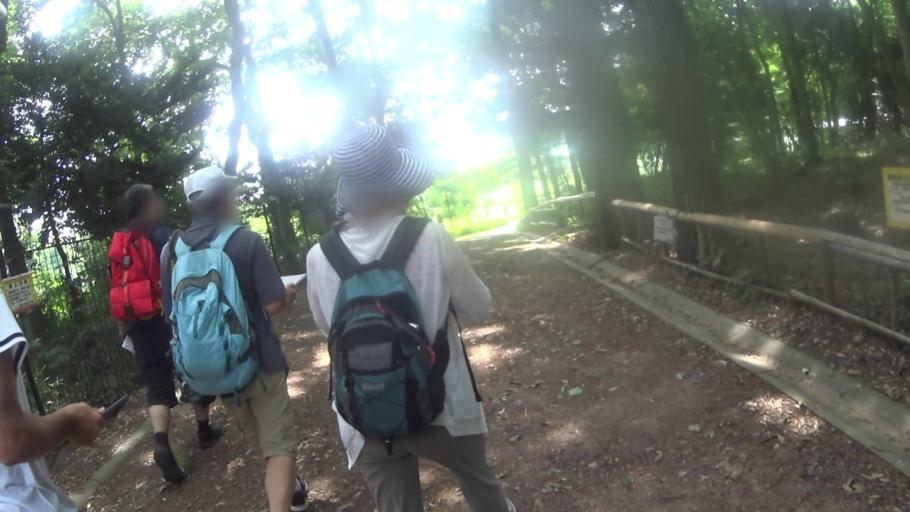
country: JP
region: Saitama
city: Ageoshimo
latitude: 35.9361
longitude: 139.5654
